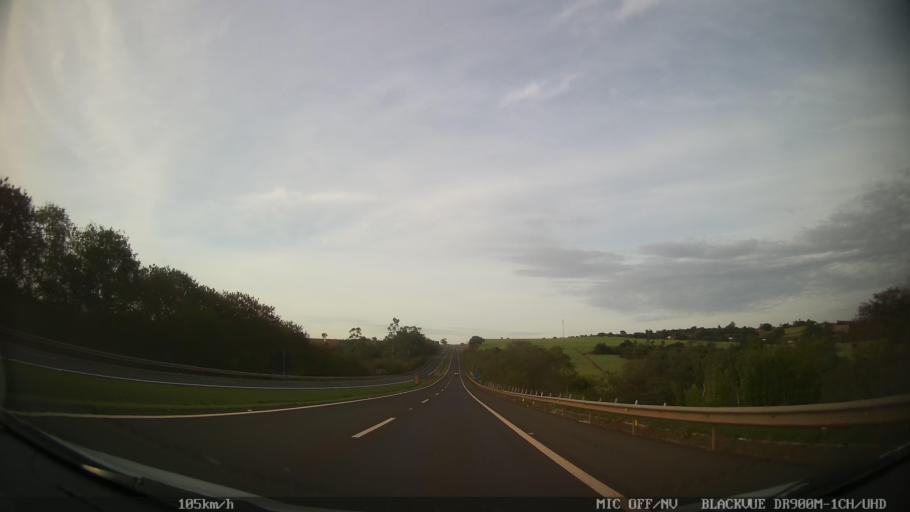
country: BR
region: Sao Paulo
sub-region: Iracemapolis
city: Iracemapolis
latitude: -22.6238
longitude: -47.4937
